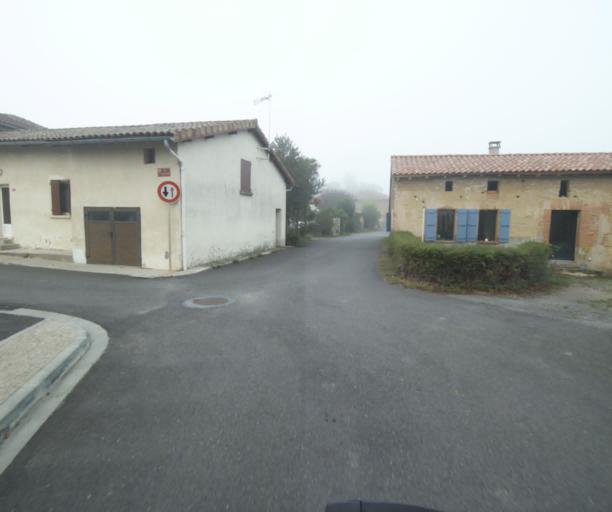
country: FR
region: Midi-Pyrenees
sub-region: Departement du Tarn-et-Garonne
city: Saint-Nauphary
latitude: 43.9360
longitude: 1.4673
